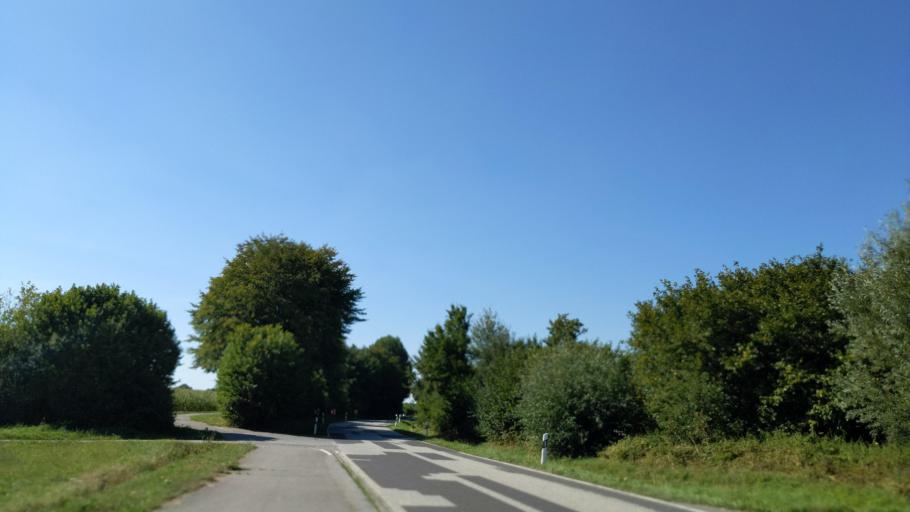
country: DE
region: Mecklenburg-Vorpommern
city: Selmsdorf
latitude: 53.8289
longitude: 10.8816
